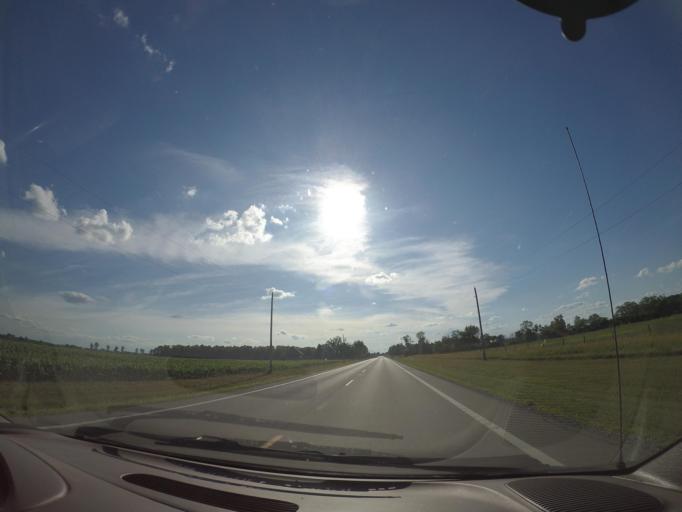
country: US
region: Ohio
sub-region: Henry County
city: Napoleon
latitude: 41.4309
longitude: -84.2141
